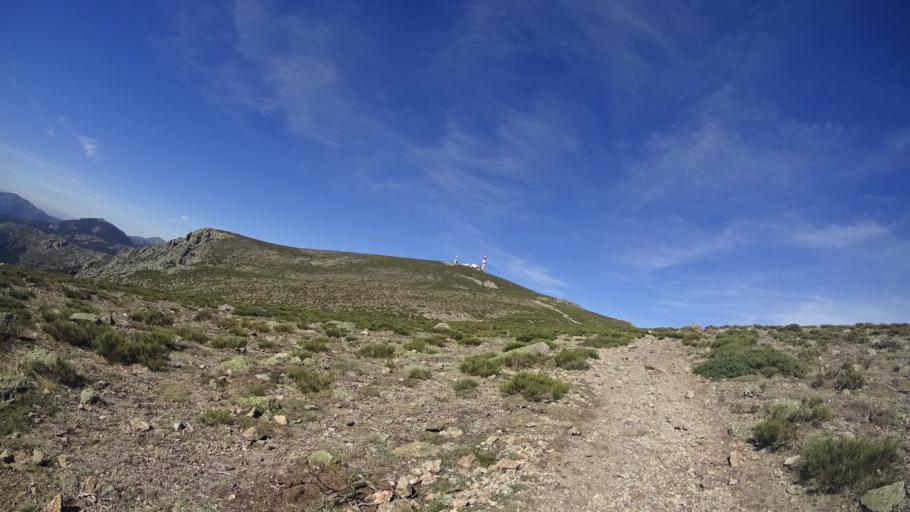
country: ES
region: Madrid
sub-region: Provincia de Madrid
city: Becerril de la Sierra
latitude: 40.7759
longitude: -3.9725
